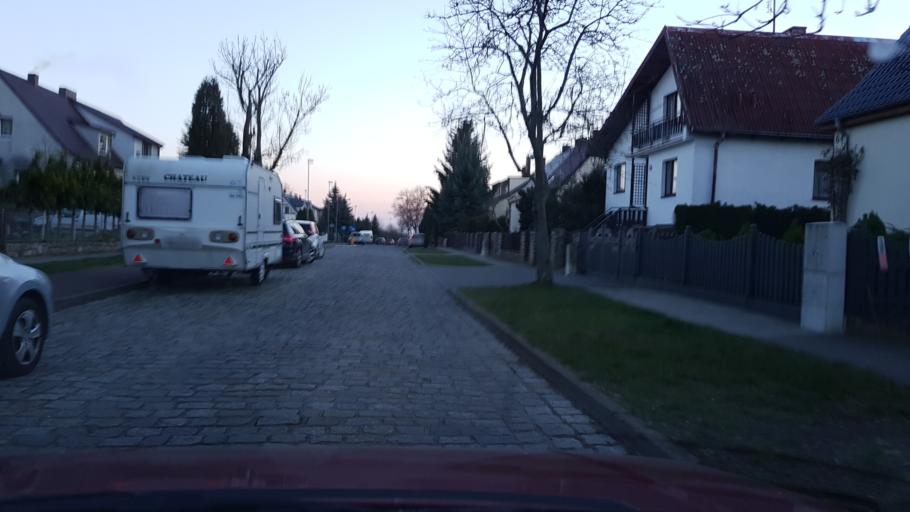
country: PL
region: West Pomeranian Voivodeship
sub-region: Szczecin
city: Szczecin
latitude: 53.4658
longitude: 14.5345
